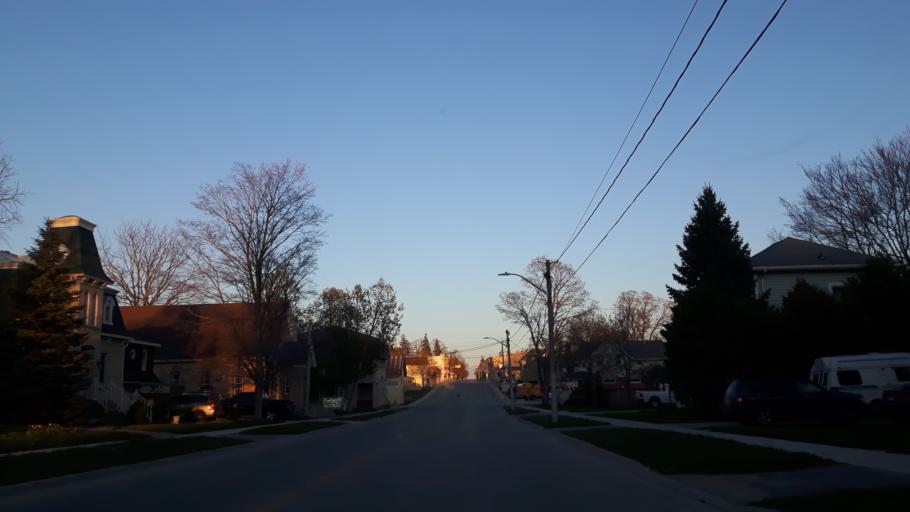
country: CA
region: Ontario
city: Bluewater
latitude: 43.6187
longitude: -81.5434
